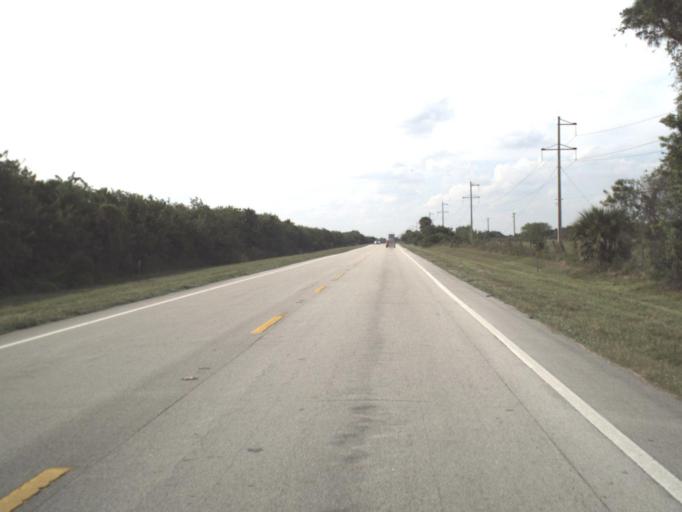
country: US
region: Florida
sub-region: Okeechobee County
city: Taylor Creek
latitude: 27.1791
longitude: -80.7077
